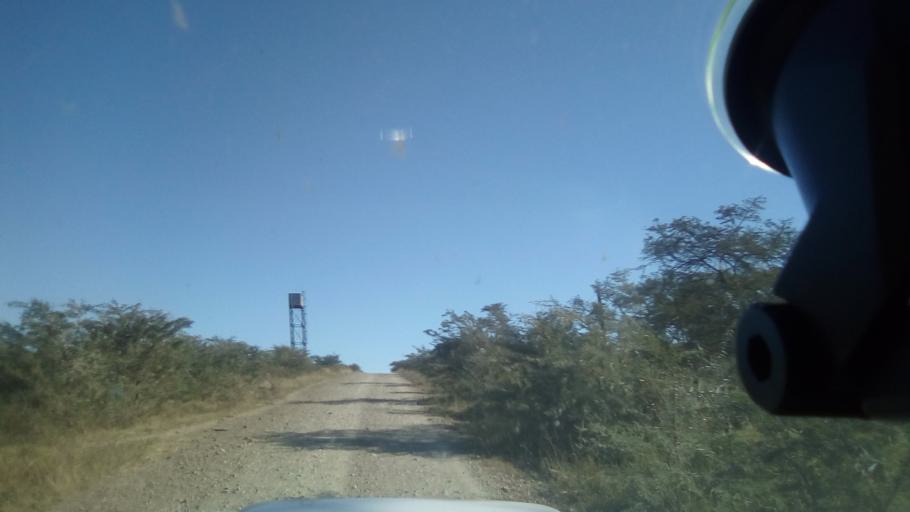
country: ZA
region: Eastern Cape
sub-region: Buffalo City Metropolitan Municipality
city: Bhisho
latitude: -32.7546
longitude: 27.3362
